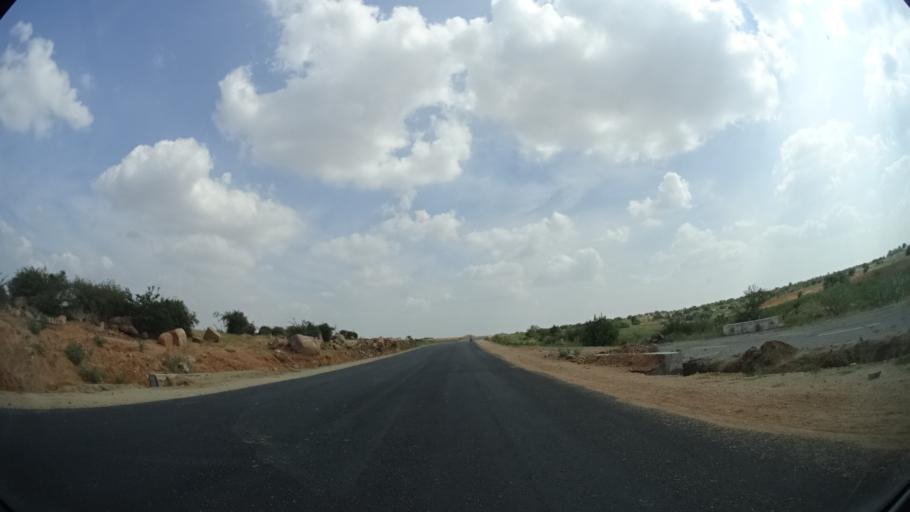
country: IN
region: Andhra Pradesh
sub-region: Anantapur
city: Uravakonda
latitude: 14.7898
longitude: 77.3647
